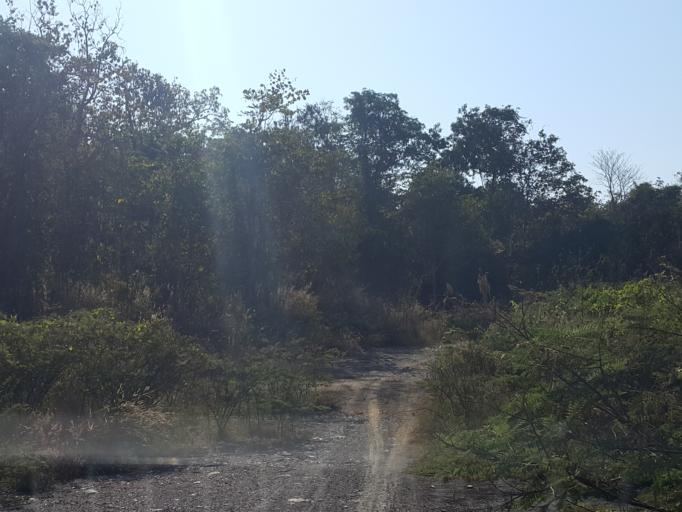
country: TH
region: Sukhothai
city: Thung Saliam
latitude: 17.3061
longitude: 99.4241
